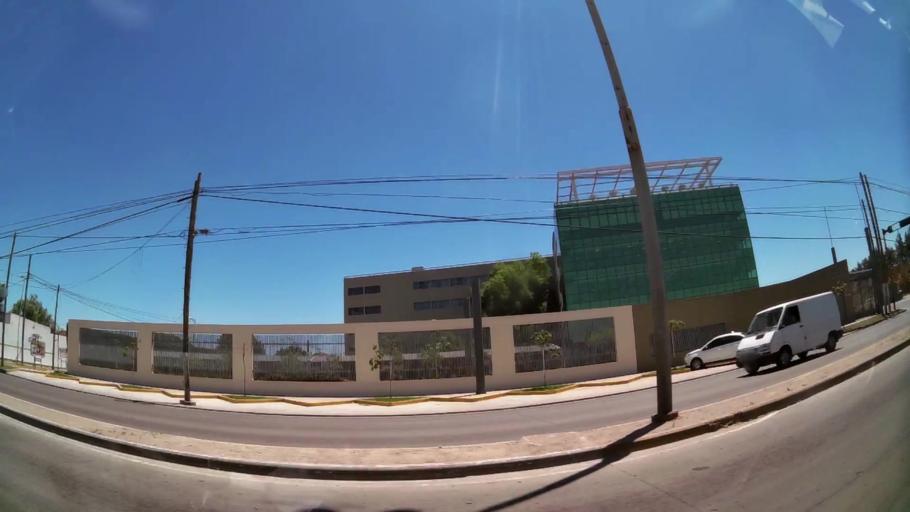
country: AR
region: Buenos Aires
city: Hurlingham
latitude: -34.5003
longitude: -58.7117
